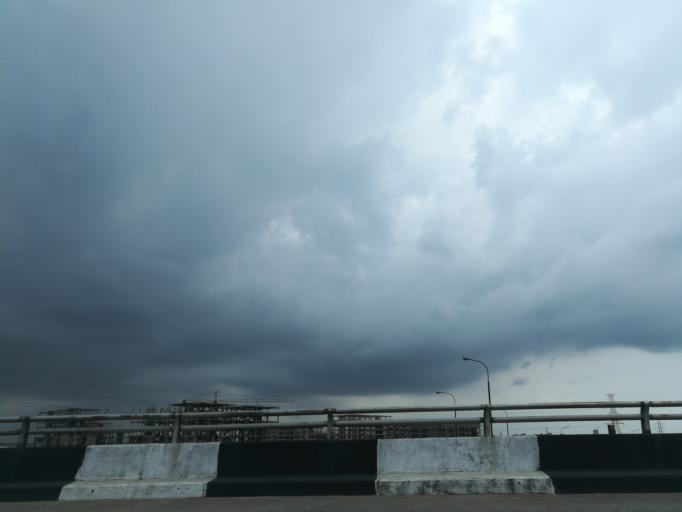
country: NG
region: Lagos
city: Lagos
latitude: 6.4623
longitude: 3.3963
